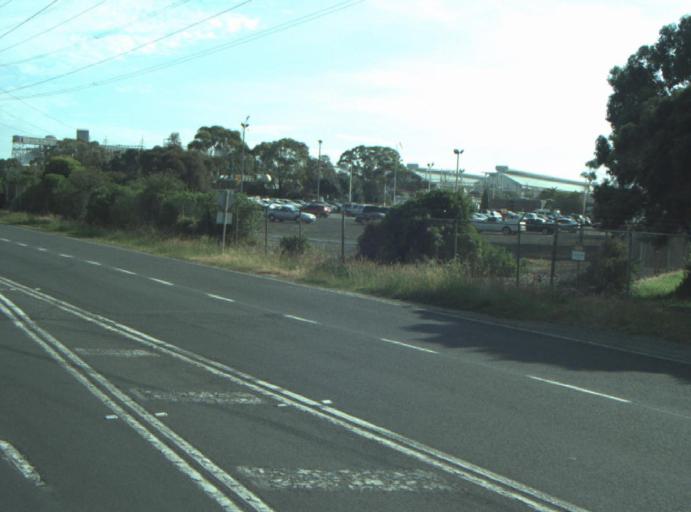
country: AU
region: Victoria
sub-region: Greater Geelong
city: East Geelong
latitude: -38.1381
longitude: 144.4200
